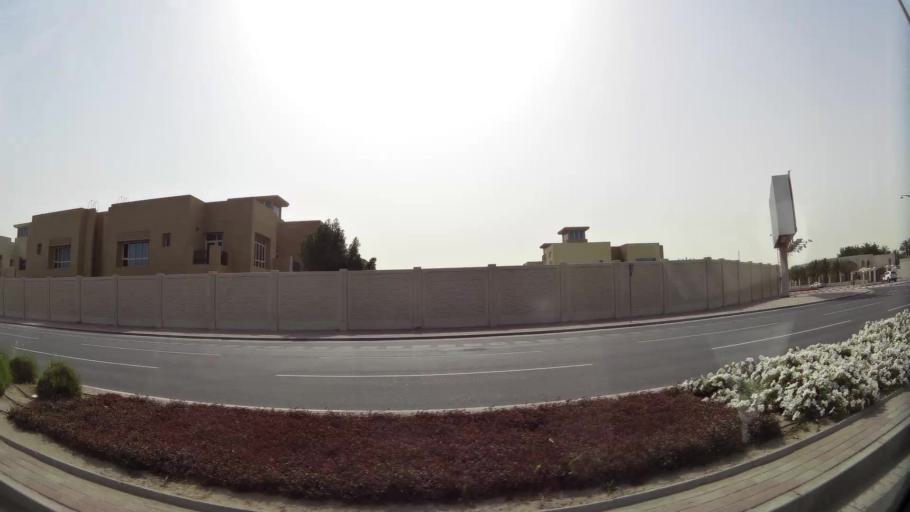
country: QA
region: Baladiyat ad Dawhah
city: Doha
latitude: 25.2655
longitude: 51.4780
